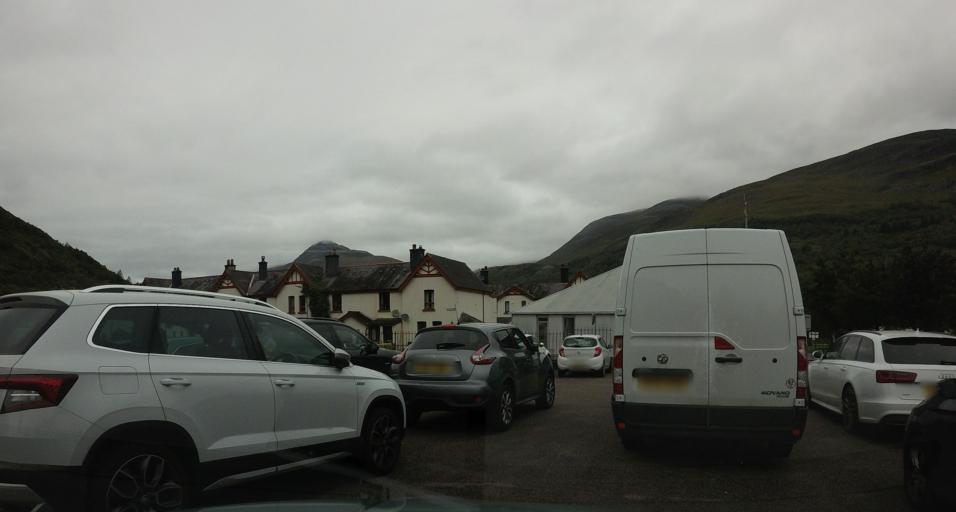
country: GB
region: Scotland
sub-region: Highland
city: Fort William
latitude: 56.7128
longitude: -4.9623
